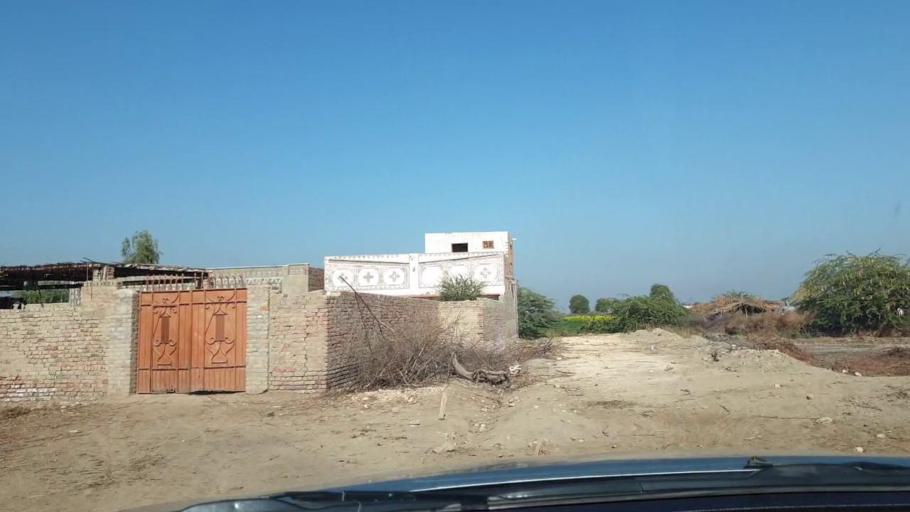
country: PK
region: Sindh
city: Jhol
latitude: 25.8845
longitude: 68.9183
